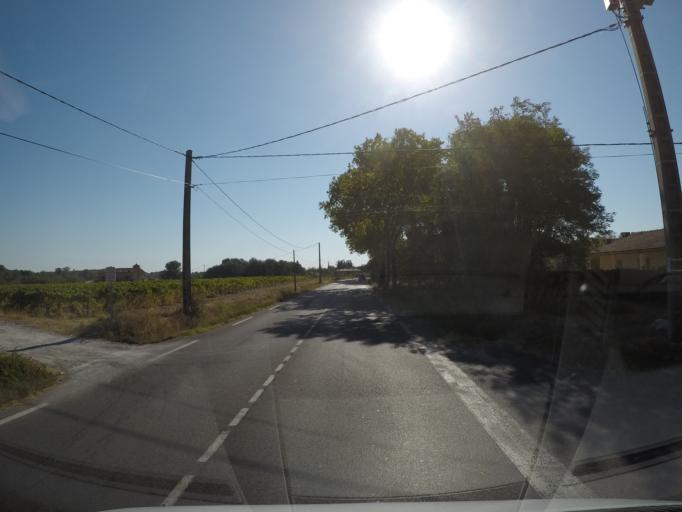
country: FR
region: Languedoc-Roussillon
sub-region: Departement du Gard
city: Boisset-et-Gaujac
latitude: 44.0340
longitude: 4.0074
